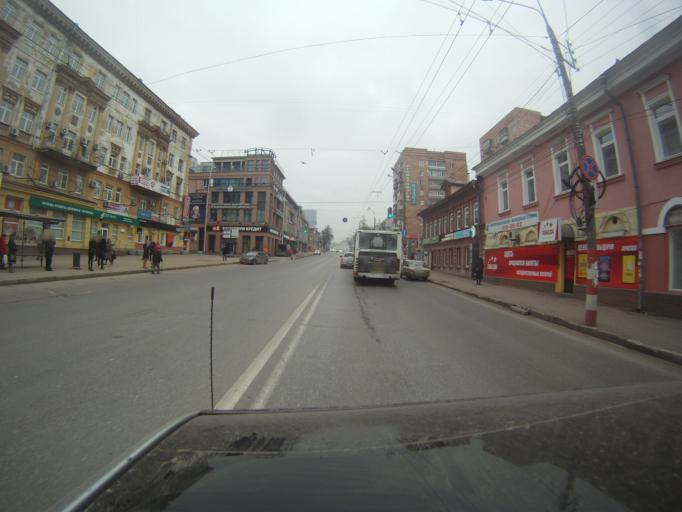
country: RU
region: Nizjnij Novgorod
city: Nizhniy Novgorod
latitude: 56.3121
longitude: 43.9892
